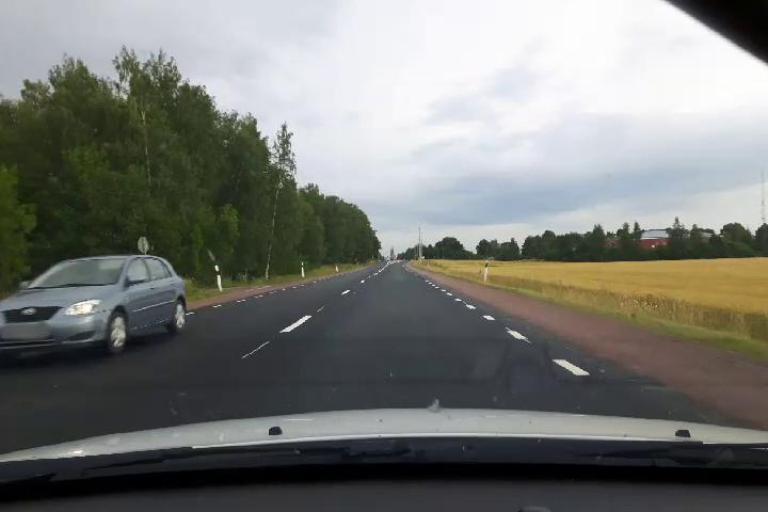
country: SE
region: Uppsala
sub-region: Uppsala Kommun
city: Gamla Uppsala
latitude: 59.8851
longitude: 17.6194
